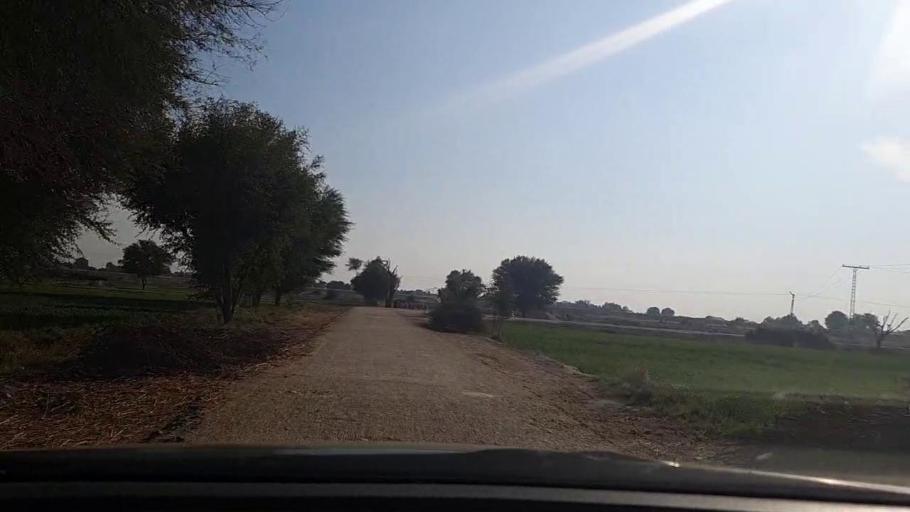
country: PK
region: Sindh
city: Sehwan
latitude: 26.3172
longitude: 68.0062
